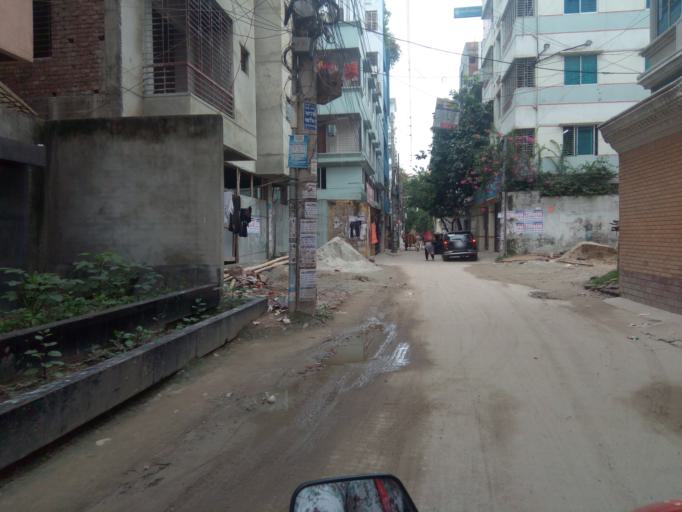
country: BD
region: Dhaka
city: Paltan
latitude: 23.7657
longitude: 90.4263
